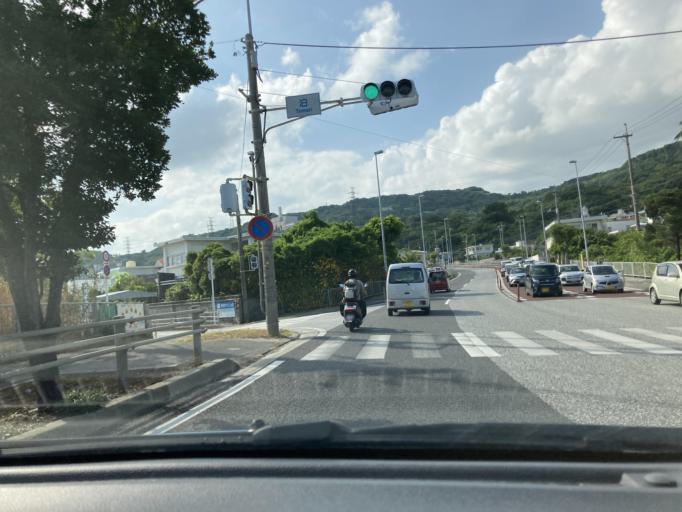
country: JP
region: Okinawa
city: Ginowan
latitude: 26.2773
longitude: 127.8064
